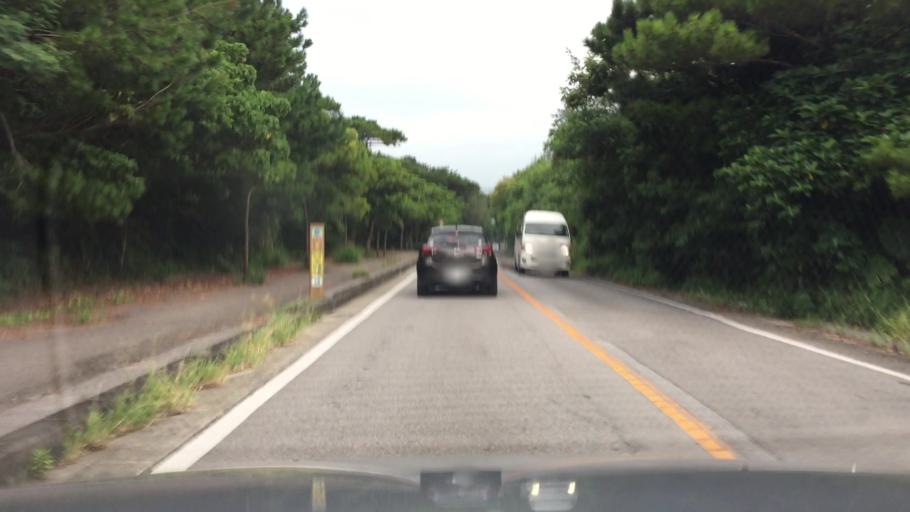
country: JP
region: Okinawa
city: Ishigaki
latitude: 24.4379
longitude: 124.1193
